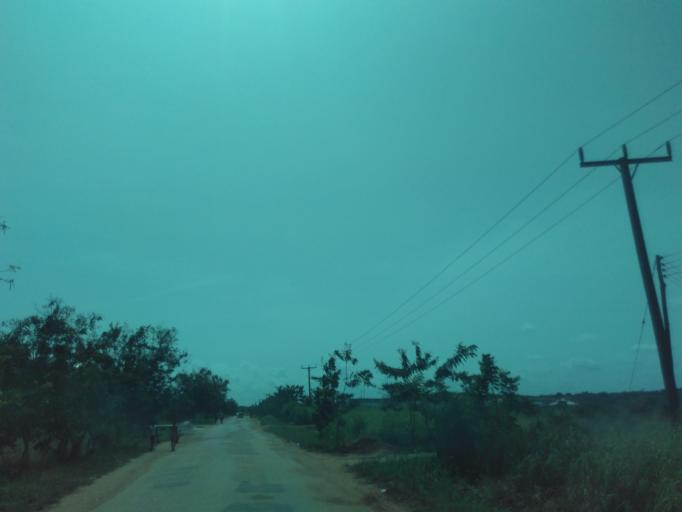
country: GH
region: Central
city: Elmina
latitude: 5.0929
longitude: -1.3771
